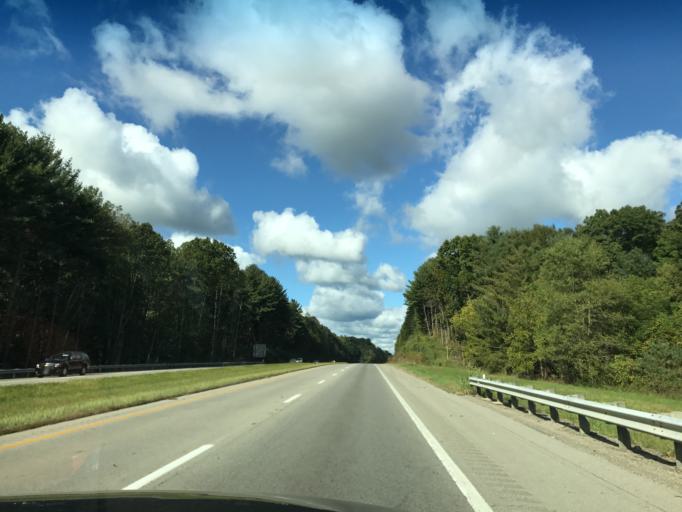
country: US
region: Ohio
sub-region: Hocking County
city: Logan
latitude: 39.5470
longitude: -82.4566
